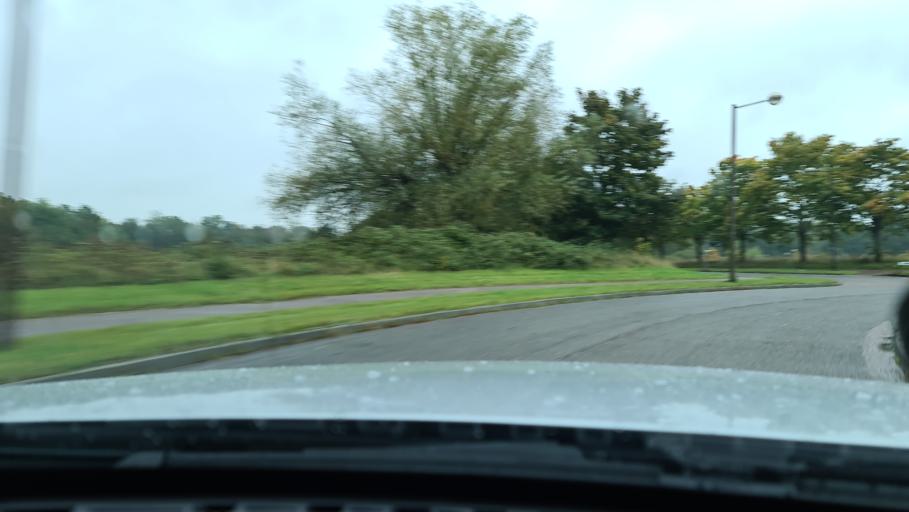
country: GB
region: England
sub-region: Milton Keynes
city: Simpson
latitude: 52.0253
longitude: -0.6999
